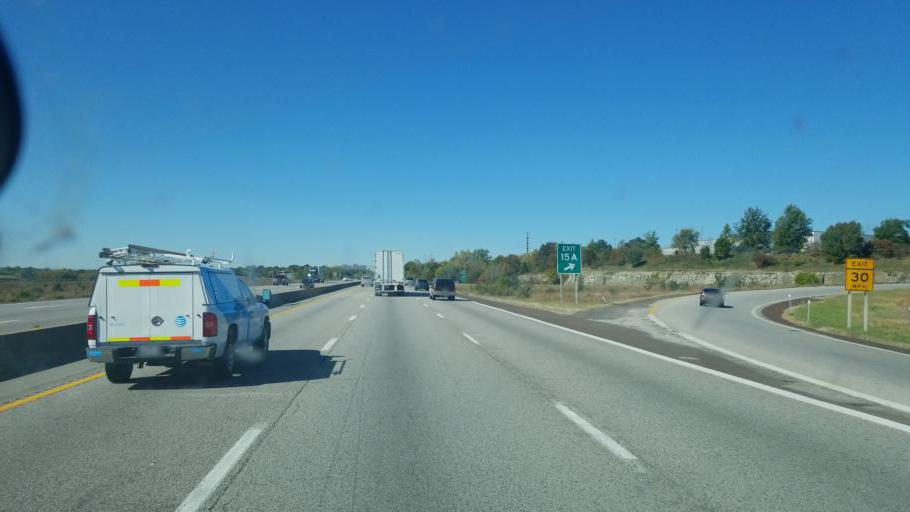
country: US
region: Missouri
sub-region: Jackson County
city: East Independence
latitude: 39.0424
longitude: -94.3639
